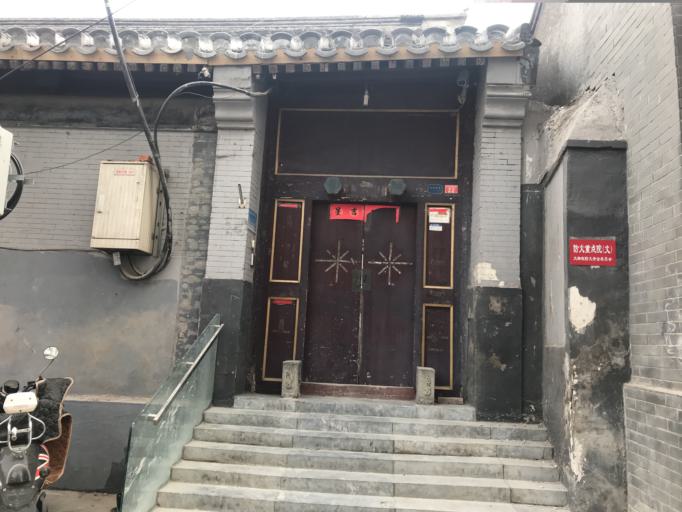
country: CN
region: Beijing
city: Beijing
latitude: 39.8924
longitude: 116.3798
